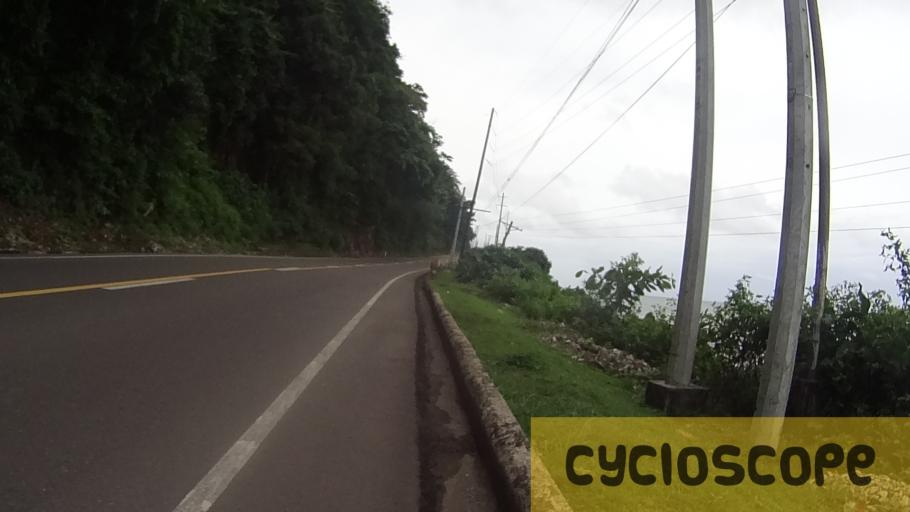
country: PH
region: Western Visayas
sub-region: Province of Aklan
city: Gibong
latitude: 11.8666
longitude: 122.0357
